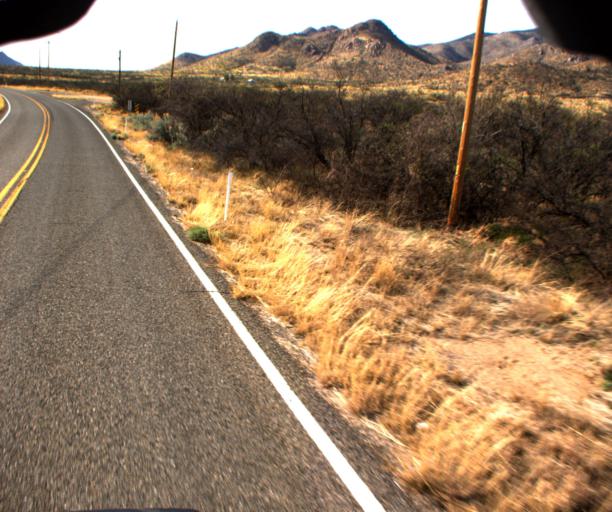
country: US
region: Arizona
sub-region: Cochise County
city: Willcox
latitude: 32.1736
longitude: -109.6030
